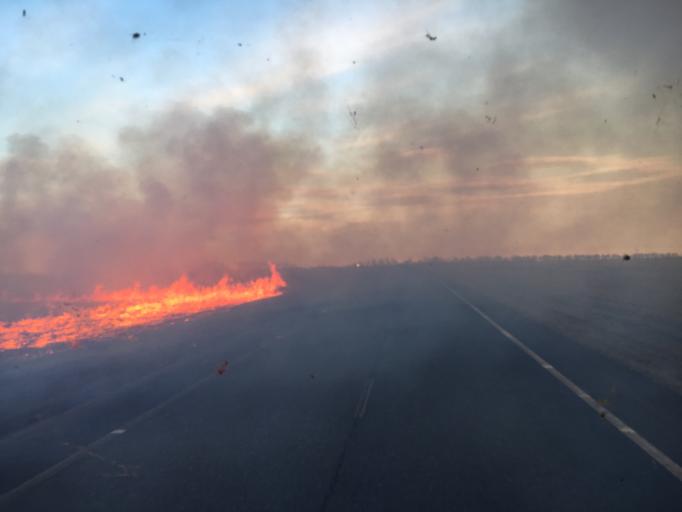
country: RU
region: Samara
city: Borskoye
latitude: 52.7692
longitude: 51.6142
